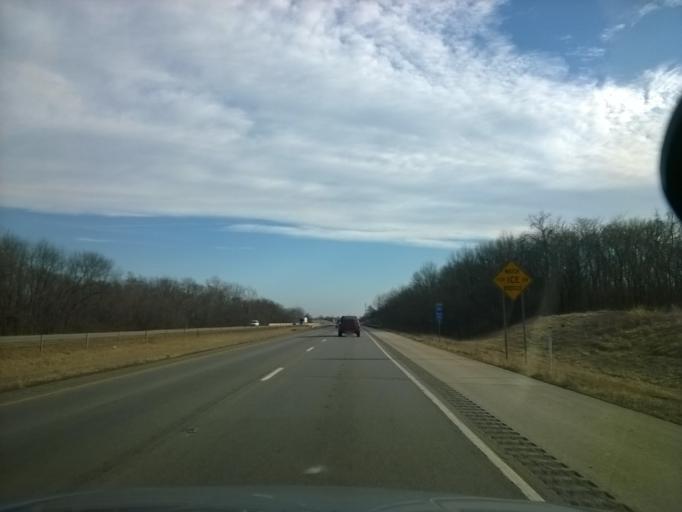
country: US
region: Indiana
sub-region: Johnson County
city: Franklin
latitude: 39.4372
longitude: -85.9833
